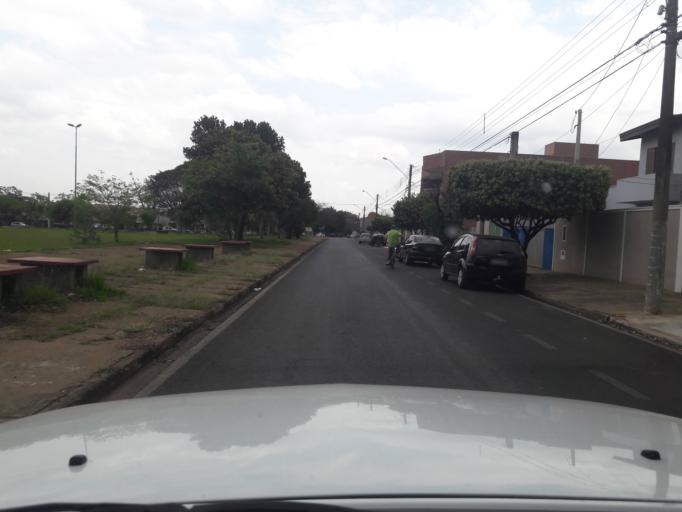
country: BR
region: Sao Paulo
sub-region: Moji-Guacu
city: Mogi-Gaucu
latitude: -22.3460
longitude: -46.9383
